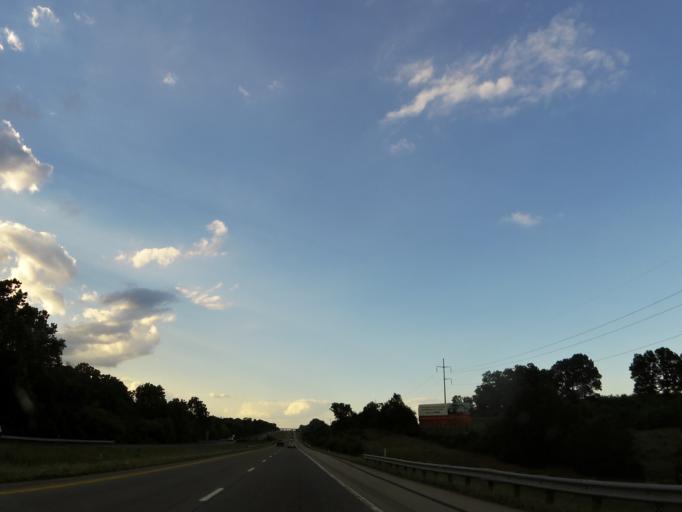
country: US
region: Tennessee
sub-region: Maury County
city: Spring Hill
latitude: 35.7202
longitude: -86.8775
